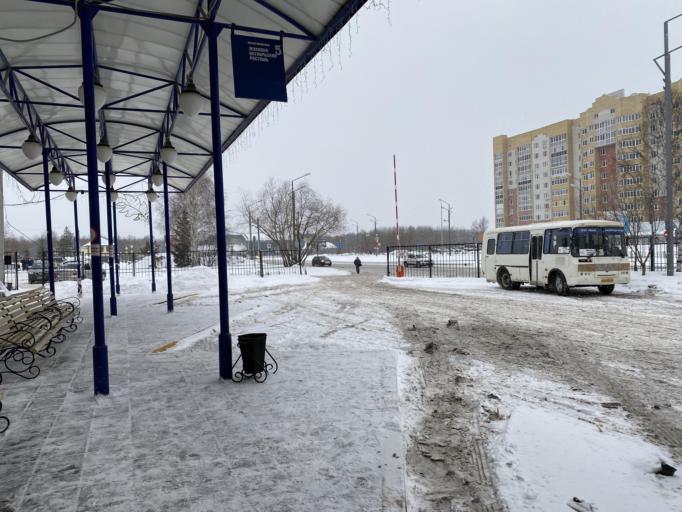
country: RU
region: Tjumen
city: Tobol'sk
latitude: 58.2275
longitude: 68.2687
